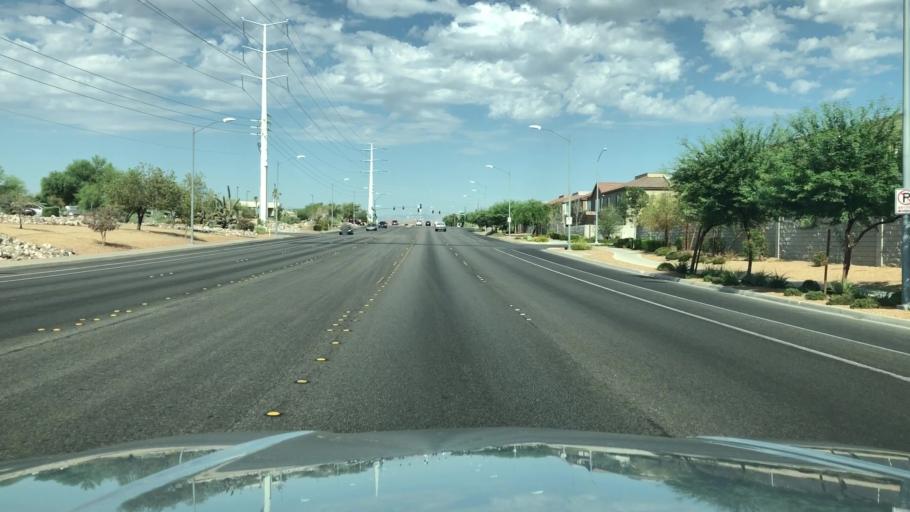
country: US
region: Nevada
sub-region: Clark County
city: Whitney
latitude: 36.0418
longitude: -115.0431
